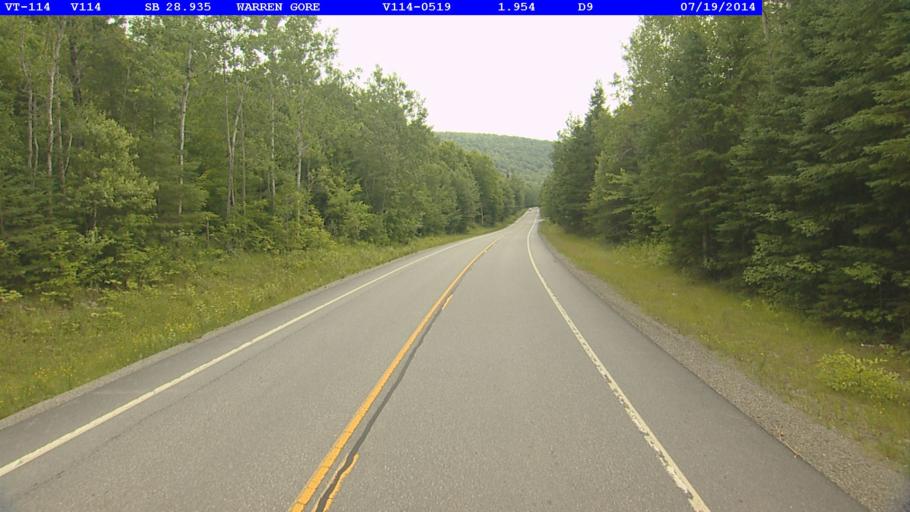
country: CA
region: Quebec
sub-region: Estrie
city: Coaticook
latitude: 44.9119
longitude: -71.8755
